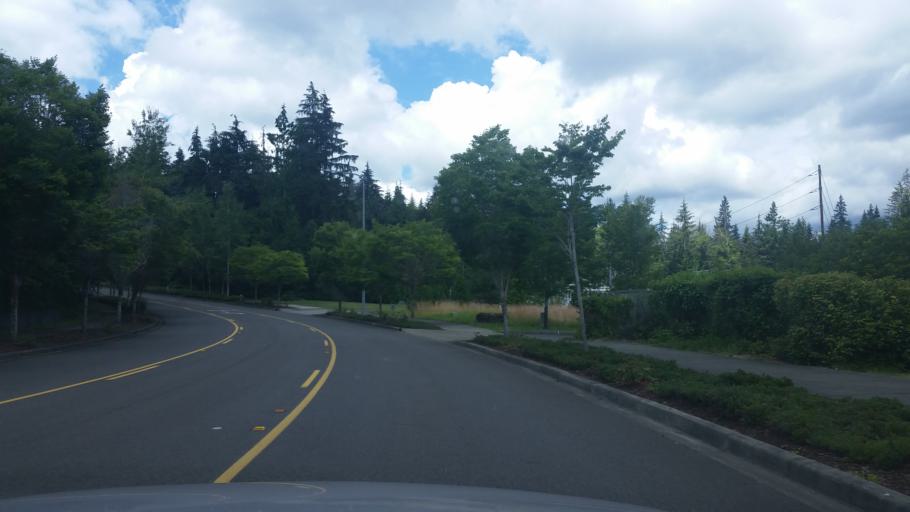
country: US
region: Washington
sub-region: King County
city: Union Hill-Novelty Hill
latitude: 47.6953
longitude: -122.0326
